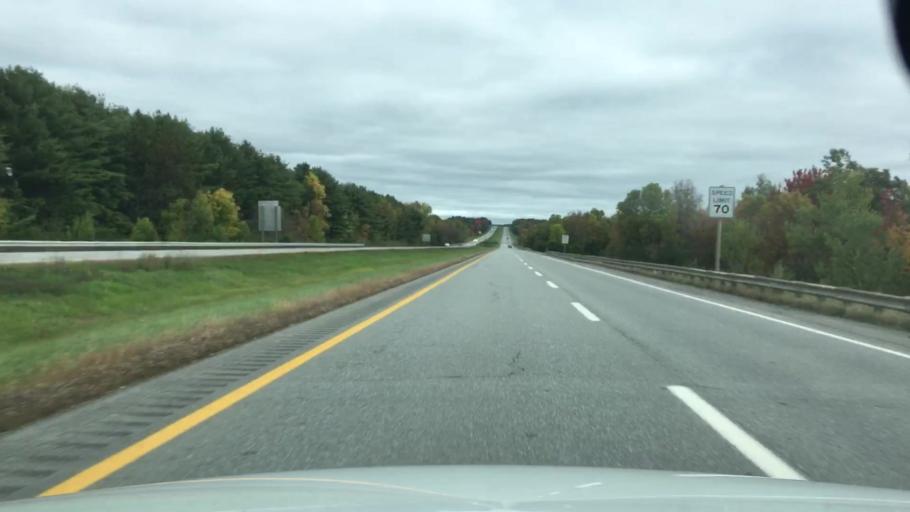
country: US
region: Maine
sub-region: Penobscot County
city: Newport
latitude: 44.8286
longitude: -69.2808
